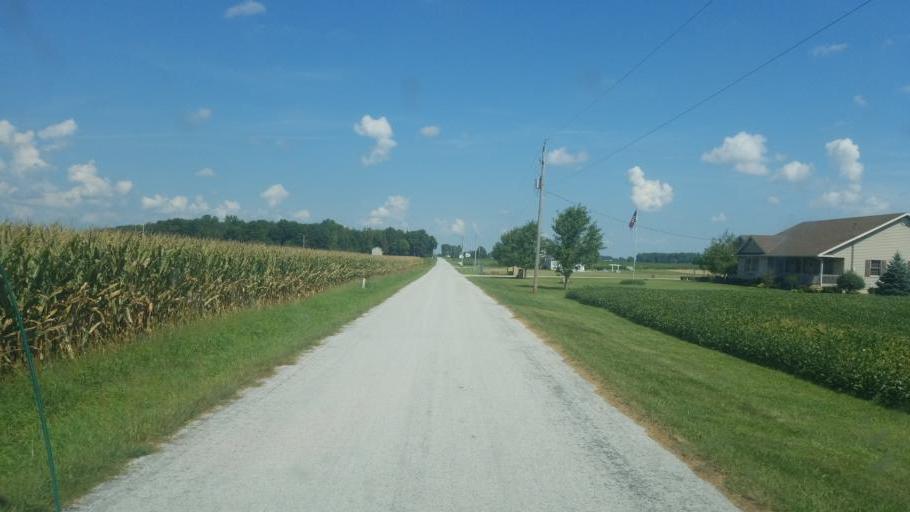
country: US
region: Ohio
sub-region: Hardin County
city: Kenton
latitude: 40.6627
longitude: -83.4957
